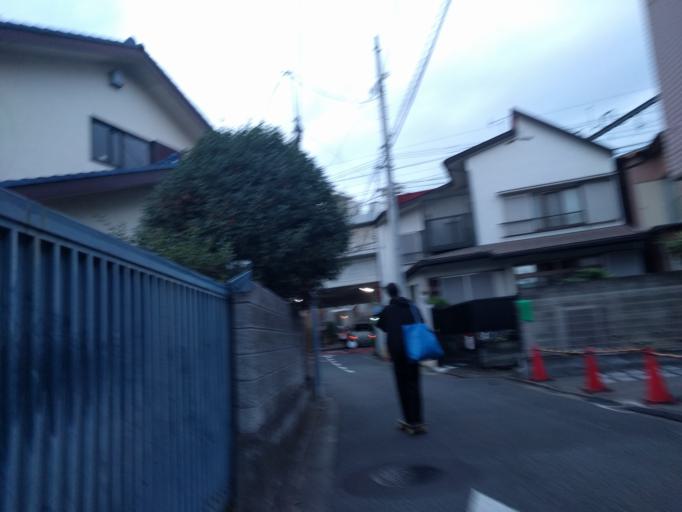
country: JP
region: Tokyo
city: Tokyo
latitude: 35.6503
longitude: 139.6352
